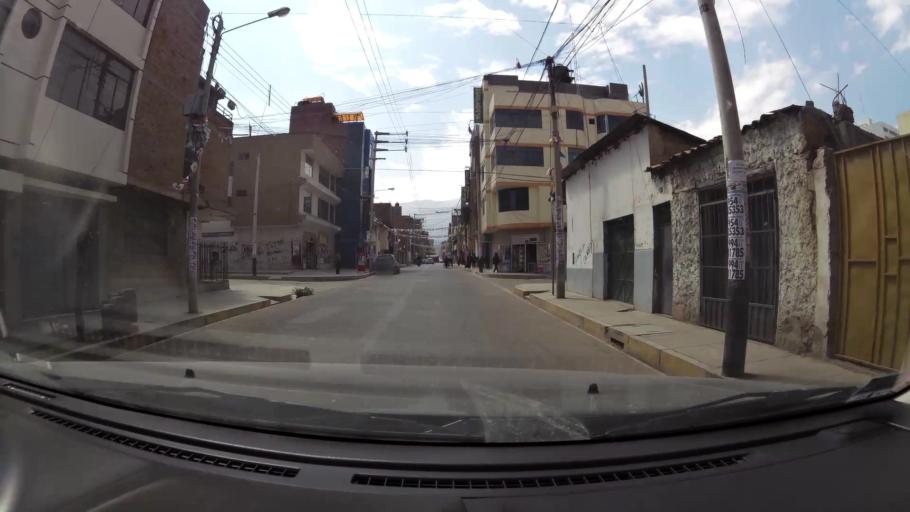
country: PE
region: Junin
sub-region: Provincia de Huancayo
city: El Tambo
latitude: -12.0727
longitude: -75.2158
